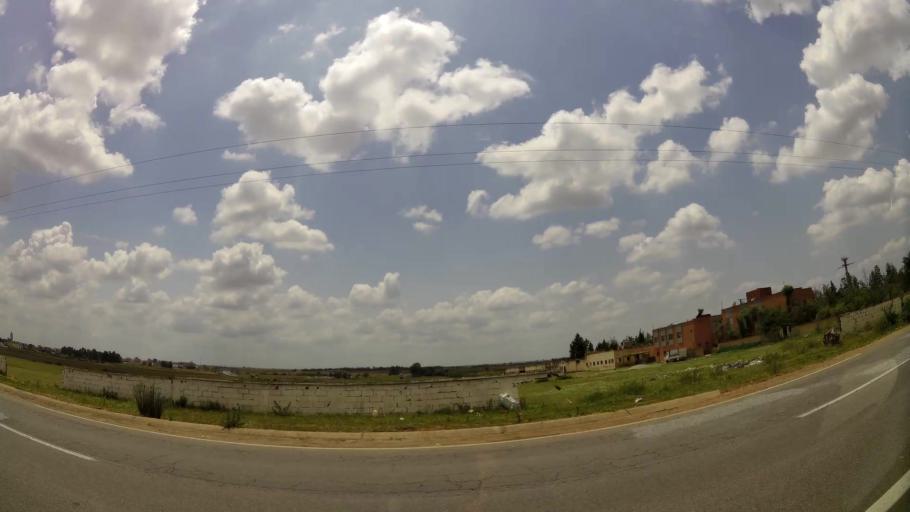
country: MA
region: Gharb-Chrarda-Beni Hssen
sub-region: Kenitra Province
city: Kenitra
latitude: 34.0145
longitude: -6.5453
